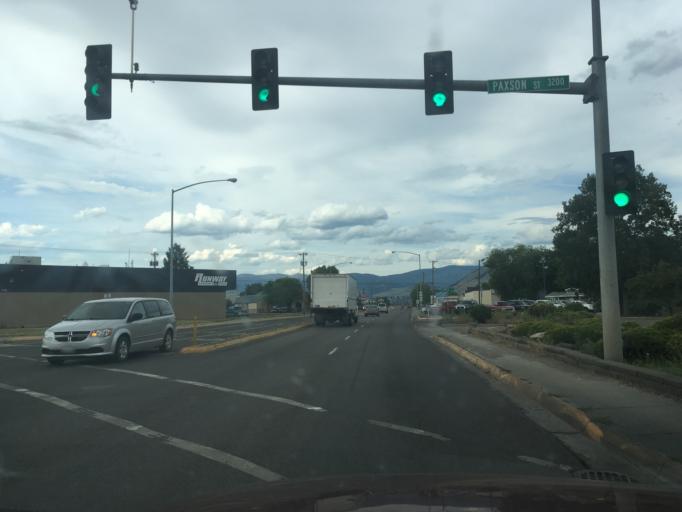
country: US
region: Montana
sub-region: Missoula County
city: Orchard Homes
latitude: 46.8412
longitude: -114.0289
